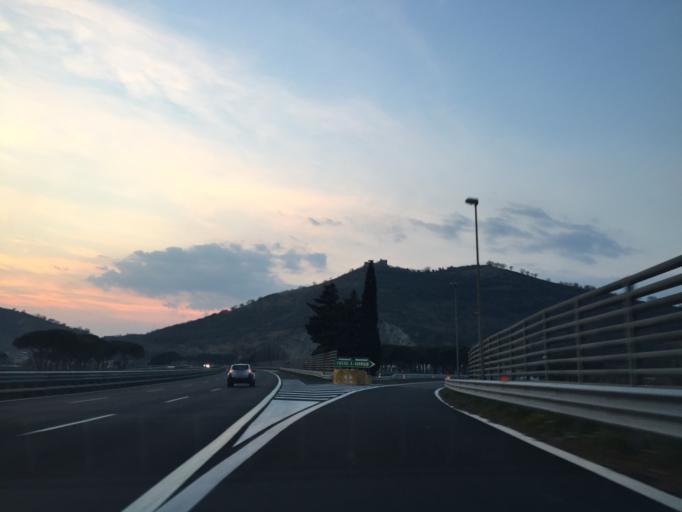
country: IT
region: Campania
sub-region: Provincia di Salerno
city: Lanzara
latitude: 40.7707
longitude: 14.6695
